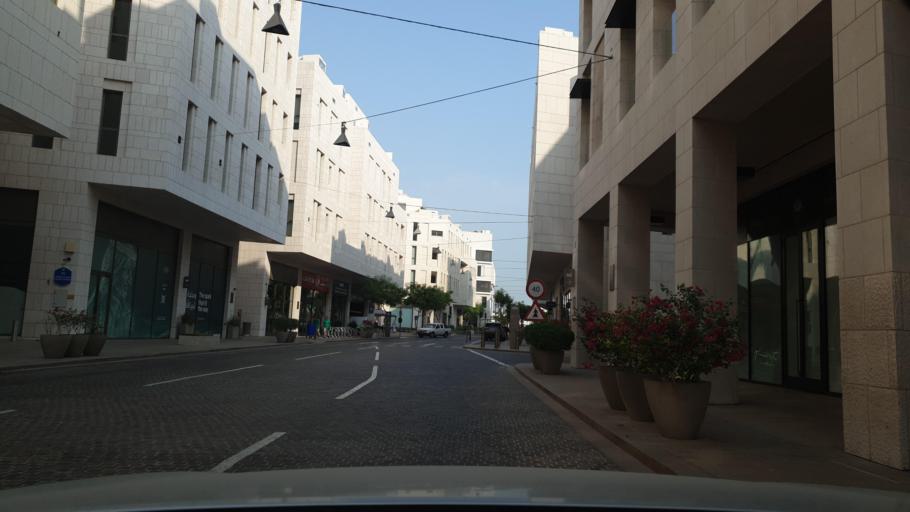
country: QA
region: Baladiyat ad Dawhah
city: Doha
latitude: 25.2858
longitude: 51.5248
